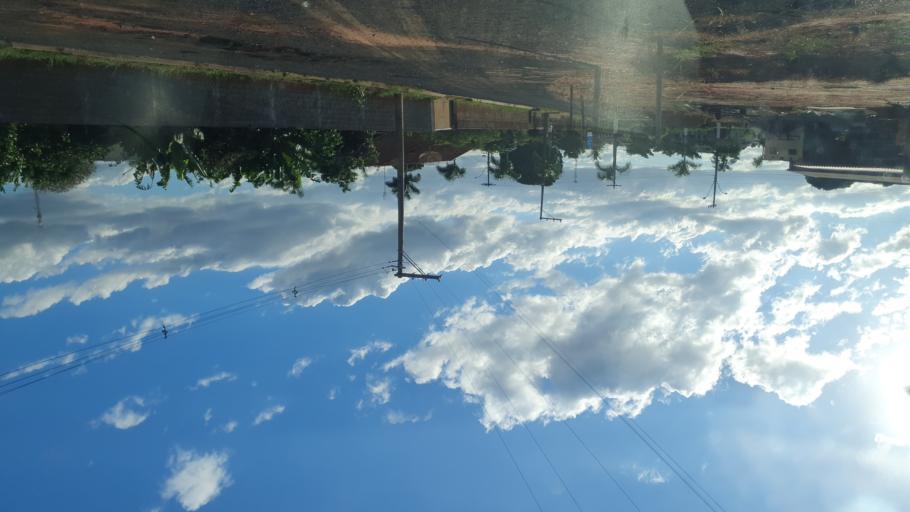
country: BR
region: Sao Paulo
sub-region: Quata
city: Quata
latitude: -22.2545
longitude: -50.7660
